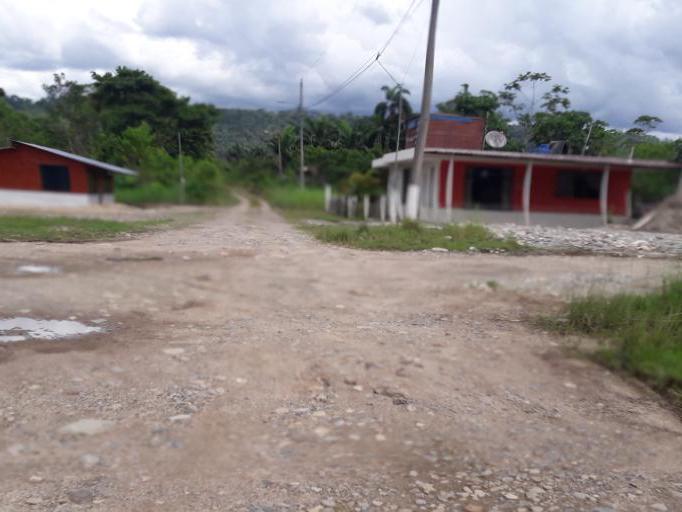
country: EC
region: Napo
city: Tena
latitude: -0.9542
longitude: -77.8169
